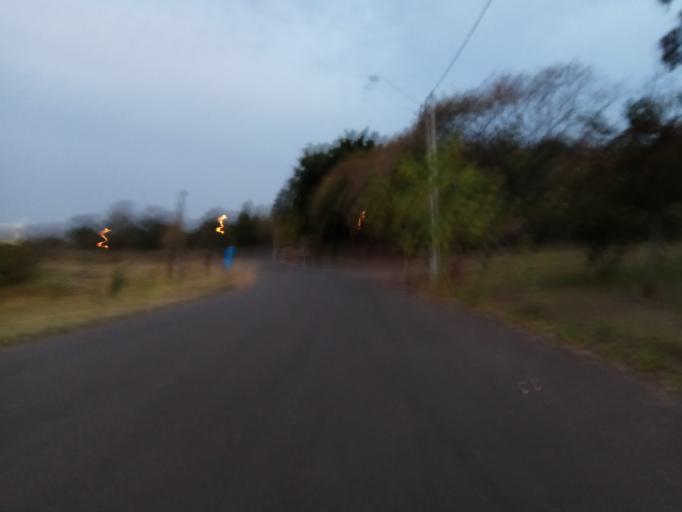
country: BR
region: Sao Paulo
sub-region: Piracicaba
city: Piracicaba
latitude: -22.7573
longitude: -47.5890
